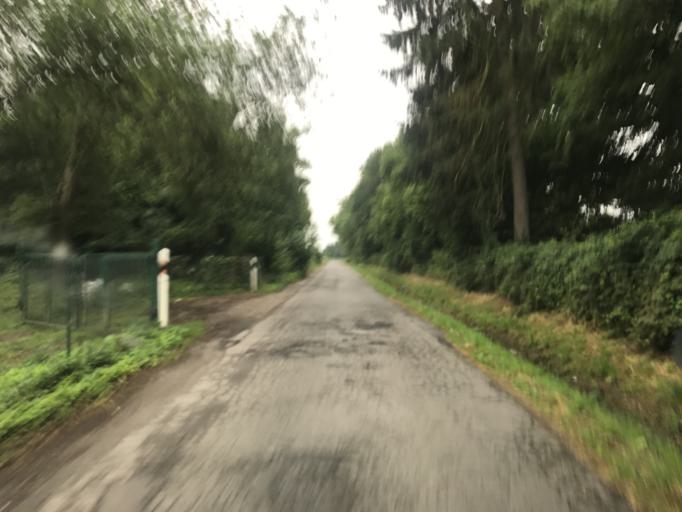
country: DE
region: North Rhine-Westphalia
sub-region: Regierungsbezirk Dusseldorf
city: Monchengladbach
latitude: 51.1679
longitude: 6.4781
